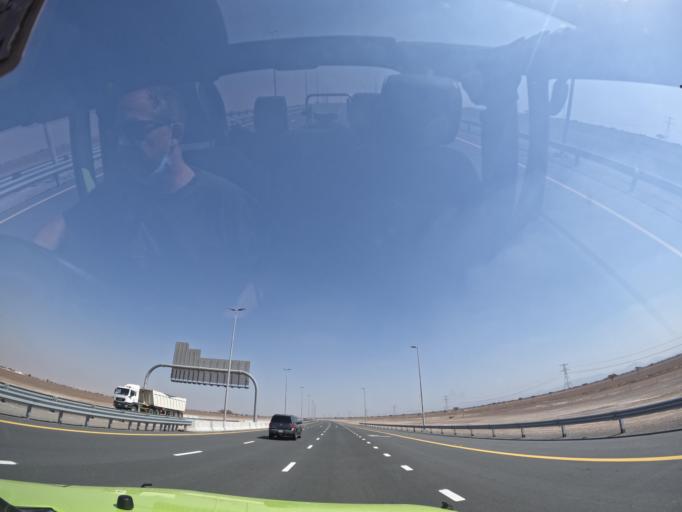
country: AE
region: Ash Shariqah
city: Adh Dhayd
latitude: 24.9383
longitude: 55.8246
